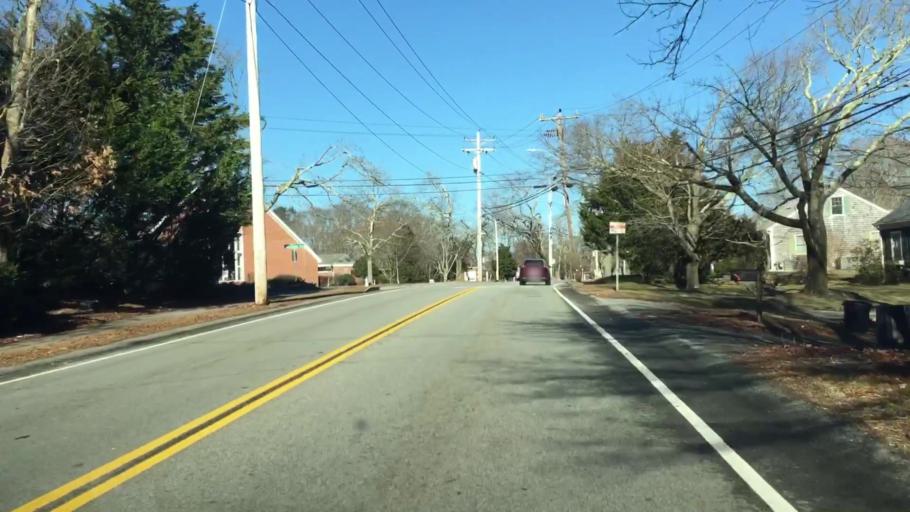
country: US
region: Massachusetts
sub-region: Barnstable County
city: Falmouth
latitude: 41.5587
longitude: -70.6108
